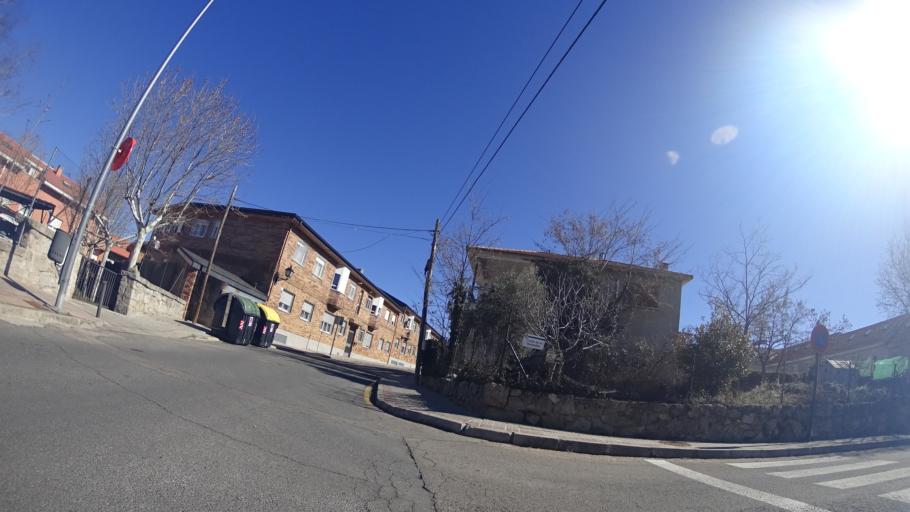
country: ES
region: Madrid
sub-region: Provincia de Madrid
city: Colmenarejo
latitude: 40.5609
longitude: -4.0151
